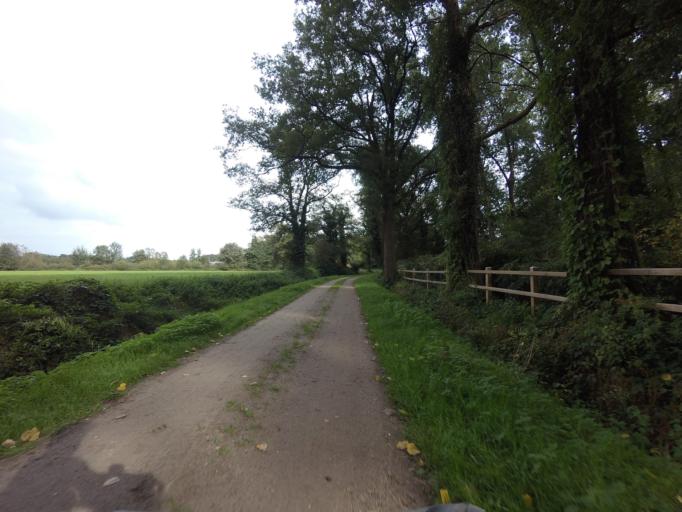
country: NL
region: Overijssel
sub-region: Gemeente Enschede
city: Enschede
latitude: 52.1930
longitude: 6.9172
